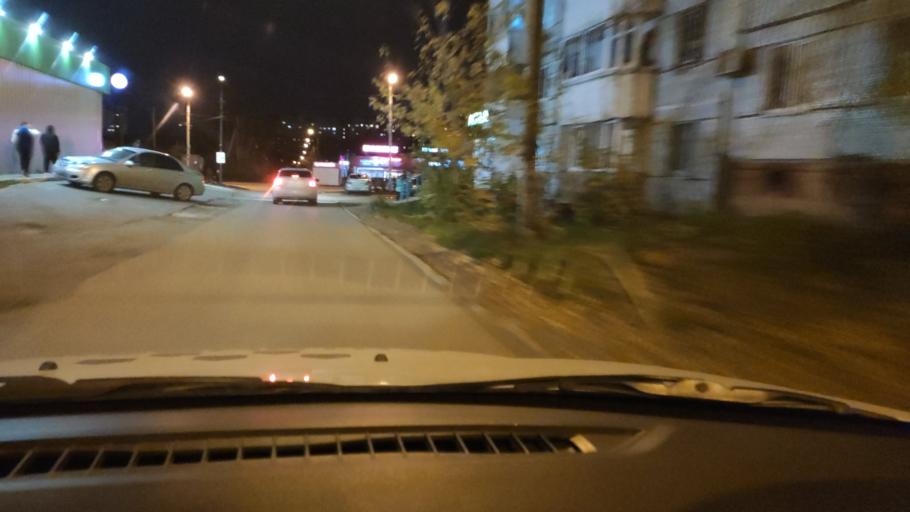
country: RU
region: Perm
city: Perm
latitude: 57.9754
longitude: 56.2005
